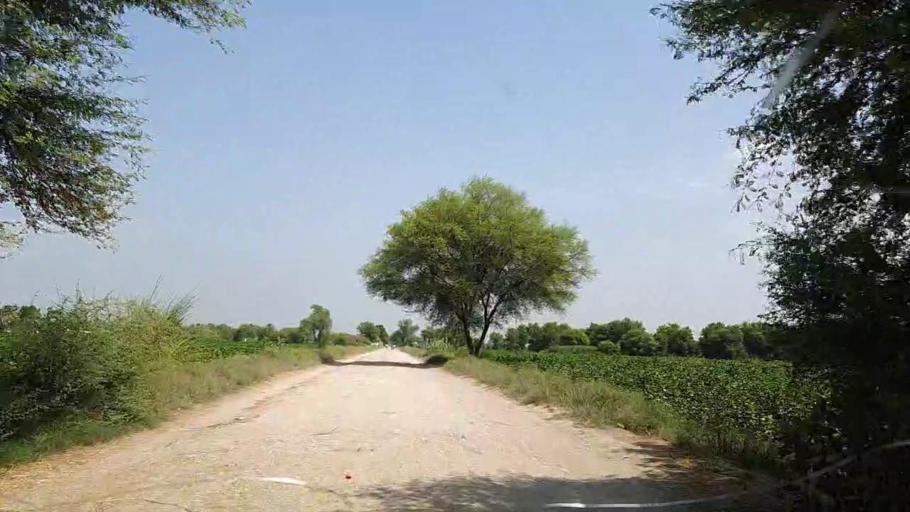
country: PK
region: Sindh
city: Adilpur
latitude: 27.8296
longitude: 69.2934
